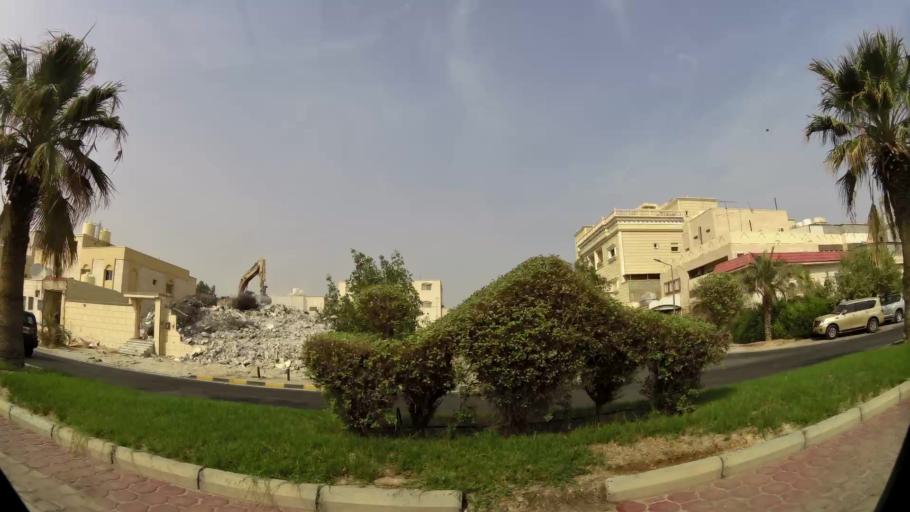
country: KW
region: Al Asimah
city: Ar Rabiyah
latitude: 29.2950
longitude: 47.9306
